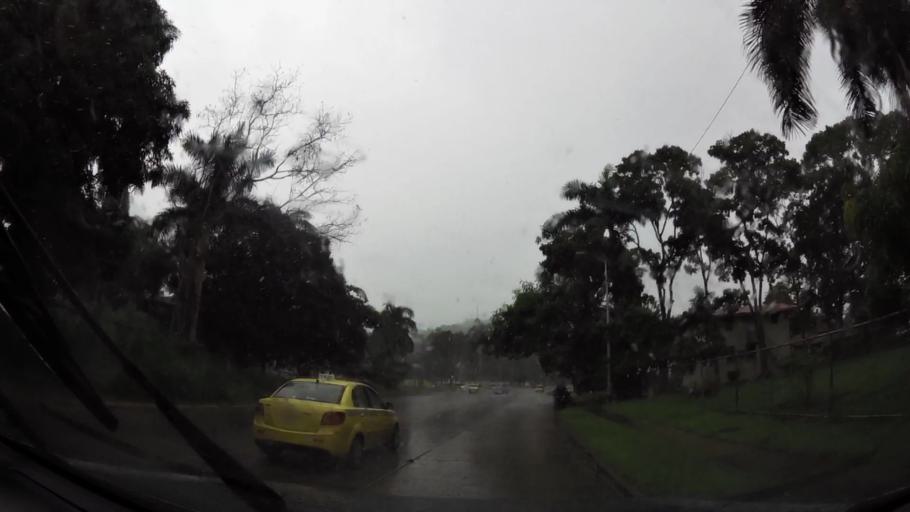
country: PA
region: Panama
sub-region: Distrito de Panama
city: Ancon
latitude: 8.9515
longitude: -79.5552
